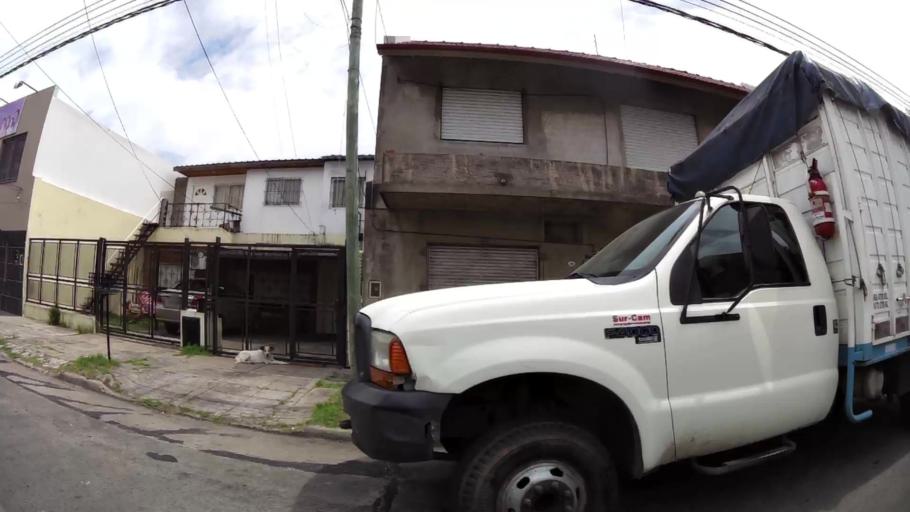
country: AR
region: Buenos Aires
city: San Justo
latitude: -34.6727
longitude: -58.5347
